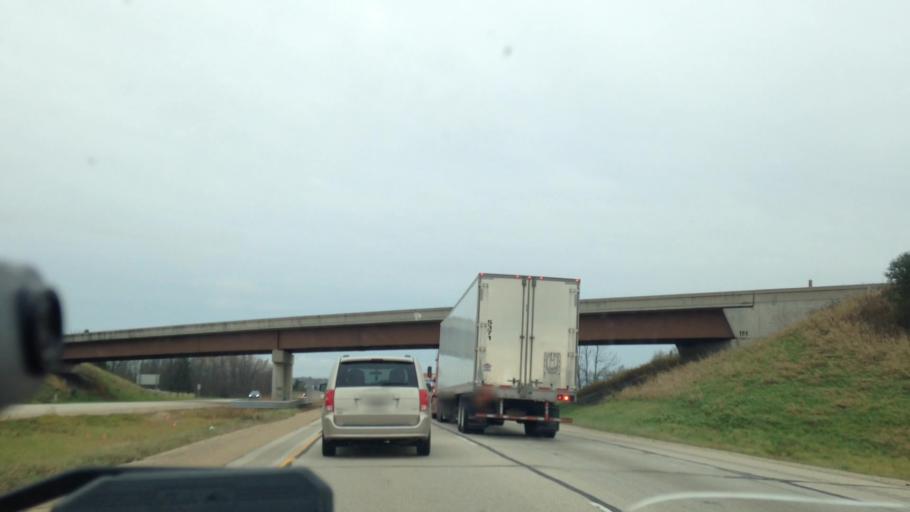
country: US
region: Wisconsin
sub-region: Washington County
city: Slinger
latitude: 43.3106
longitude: -88.2320
